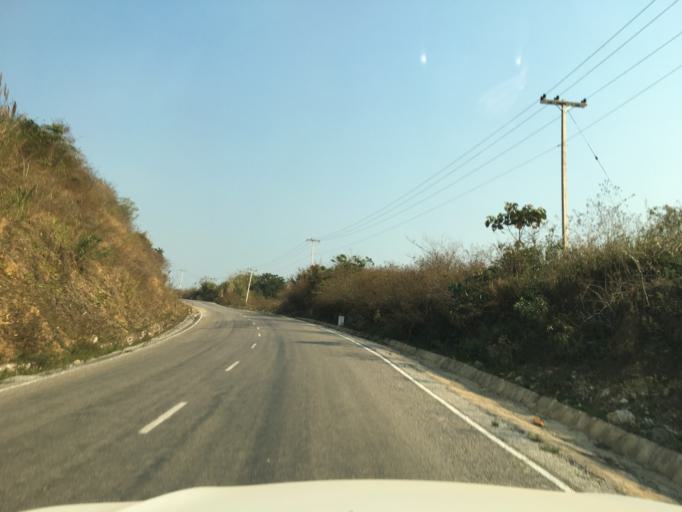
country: LA
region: Houaphan
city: Xam Nua
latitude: 20.5694
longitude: 104.0510
